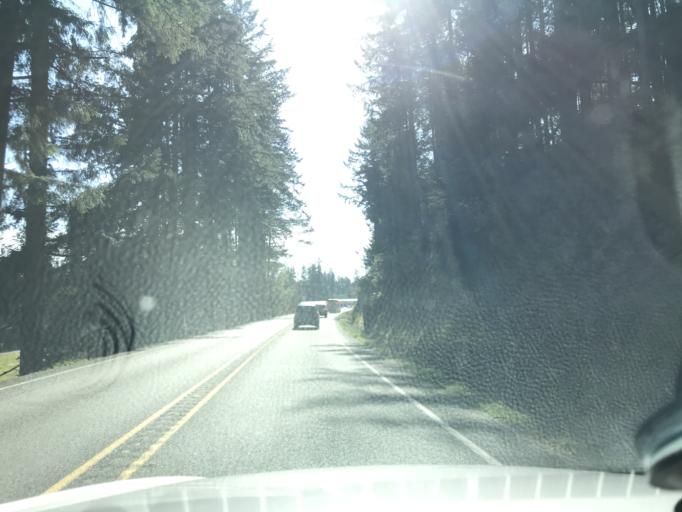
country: US
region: Washington
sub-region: Pierce County
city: Key Center
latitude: 47.3430
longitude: -122.7437
